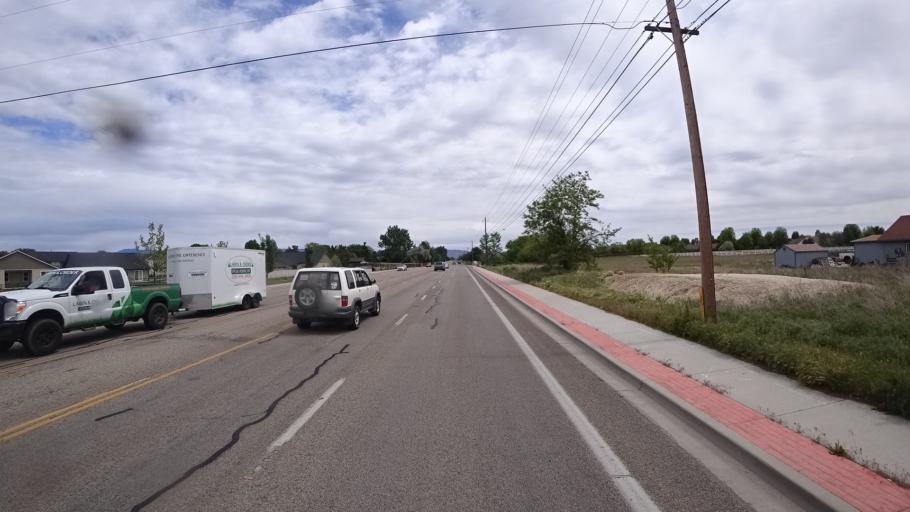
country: US
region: Idaho
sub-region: Ada County
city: Meridian
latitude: 43.5902
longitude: -116.3264
